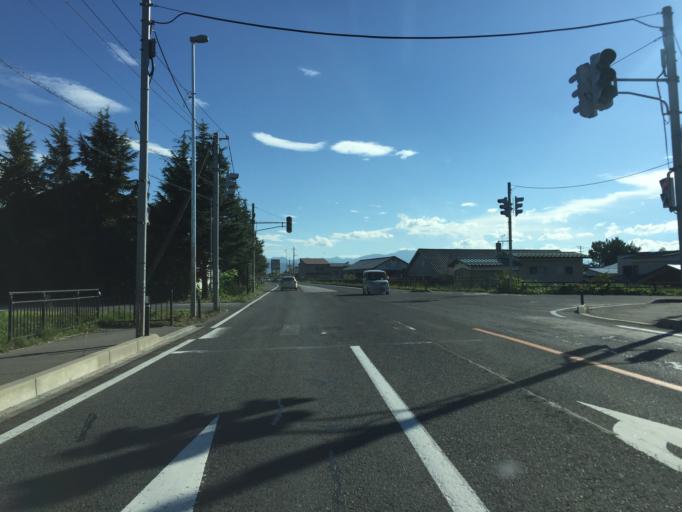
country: JP
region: Yamagata
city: Takahata
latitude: 37.9855
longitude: 140.1400
